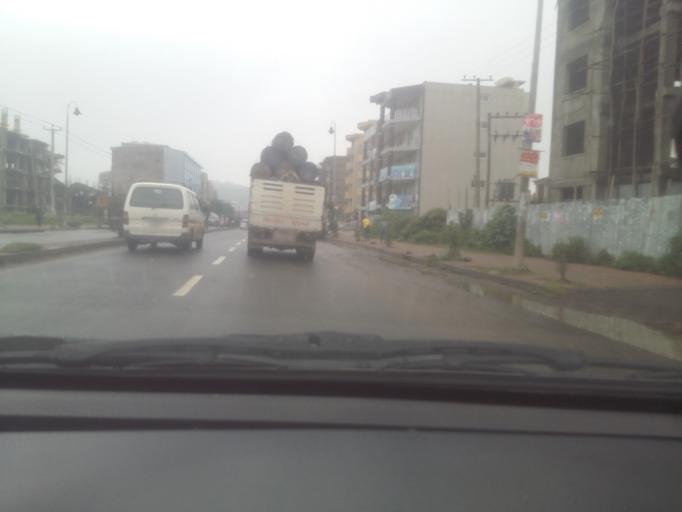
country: ET
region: Adis Abeba
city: Addis Ababa
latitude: 8.9512
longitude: 38.7178
